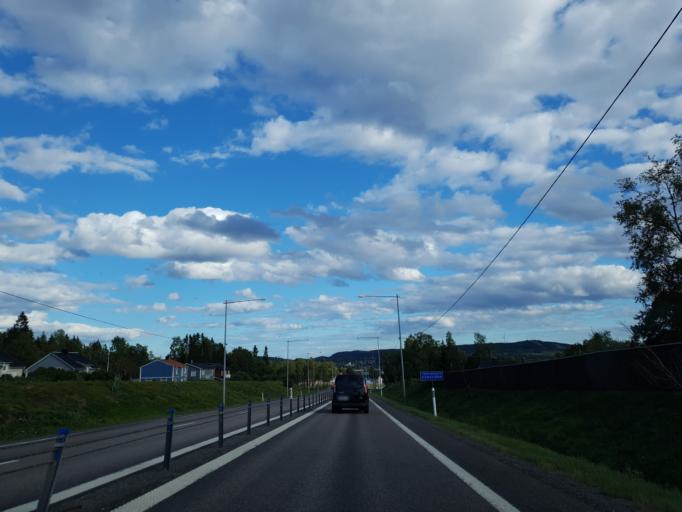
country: SE
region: Vaesternorrland
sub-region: Haernoesands Kommun
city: Haernoesand
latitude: 62.6458
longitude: 17.9035
